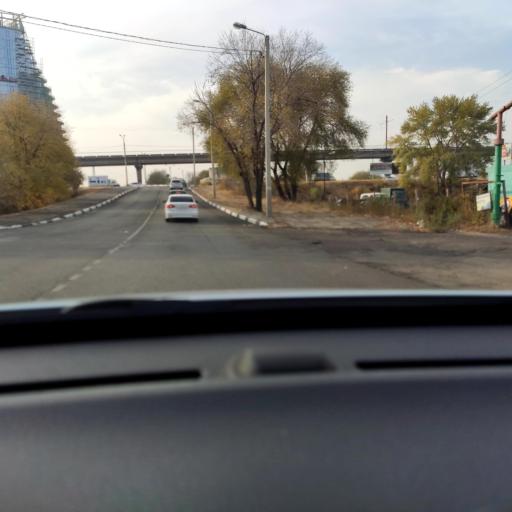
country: RU
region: Voronezj
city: Voronezh
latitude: 51.6901
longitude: 39.2518
